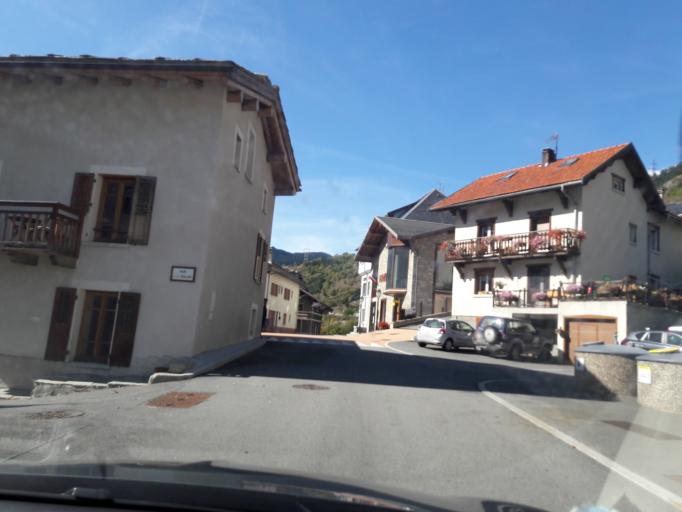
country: FR
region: Rhone-Alpes
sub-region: Departement de la Savoie
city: Modane
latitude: 45.2140
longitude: 6.6971
